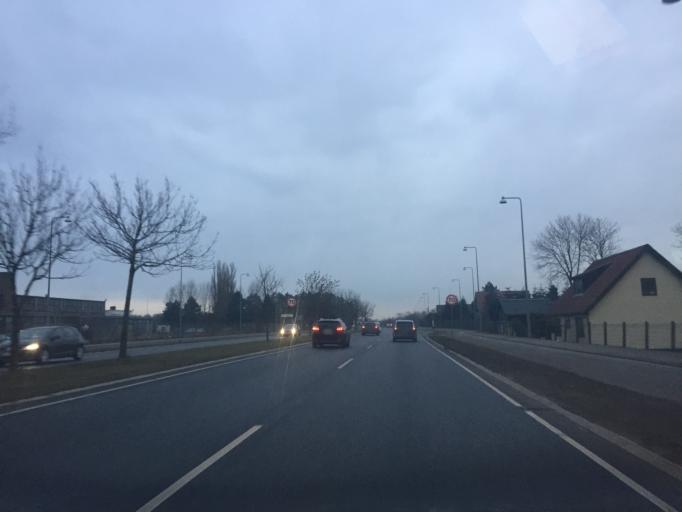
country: DK
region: Zealand
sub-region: Solrod Kommune
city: Solrod
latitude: 55.5043
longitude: 12.1994
